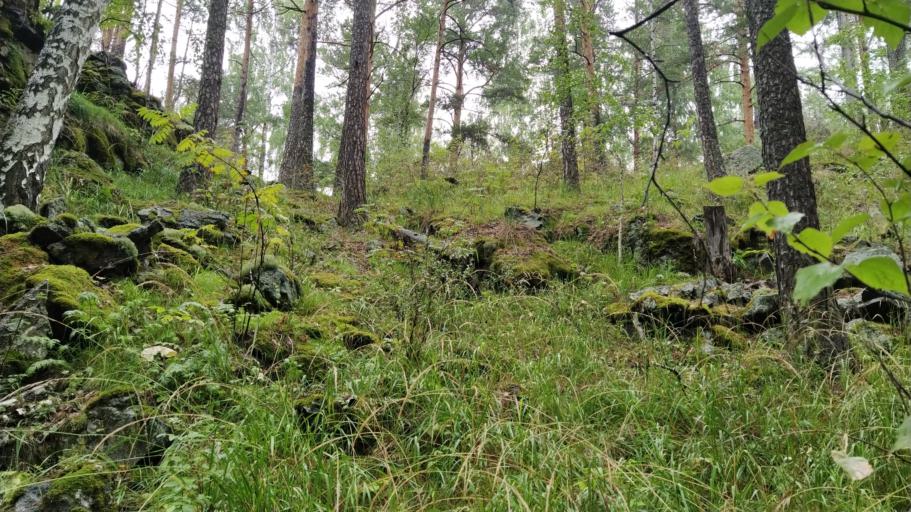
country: RU
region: Sverdlovsk
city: Zyuzel'skiy
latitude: 56.5303
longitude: 59.9843
